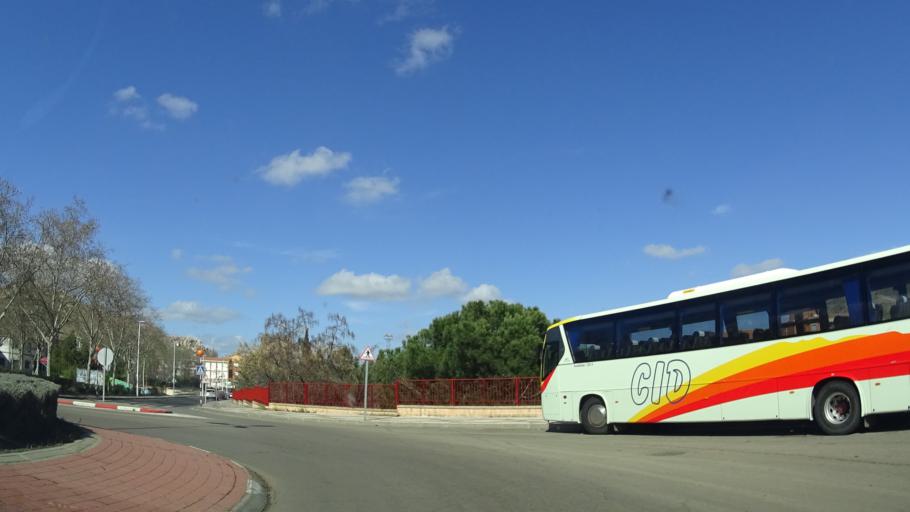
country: ES
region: Castille-La Mancha
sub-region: Provincia de Ciudad Real
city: Puertollano
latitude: 38.6889
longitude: -4.1133
